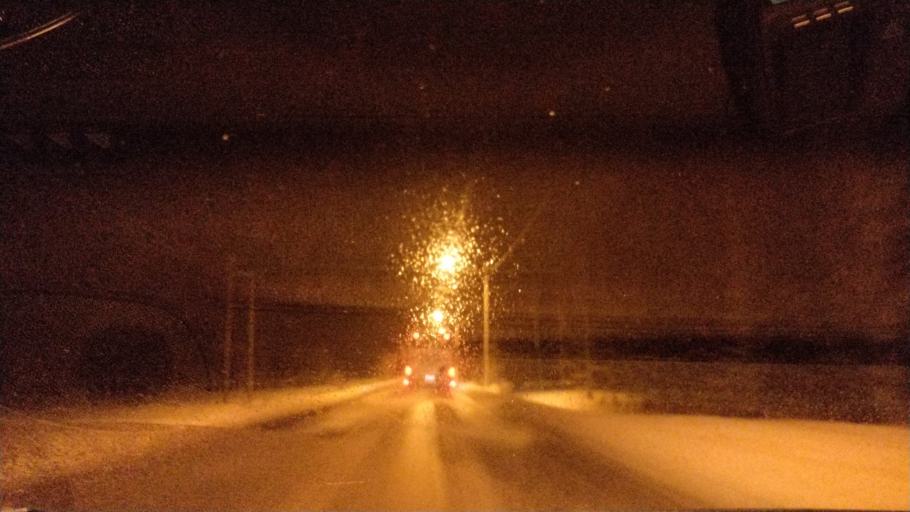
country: FI
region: Lapland
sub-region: Rovaniemi
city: Rovaniemi
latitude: 66.2937
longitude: 25.3508
